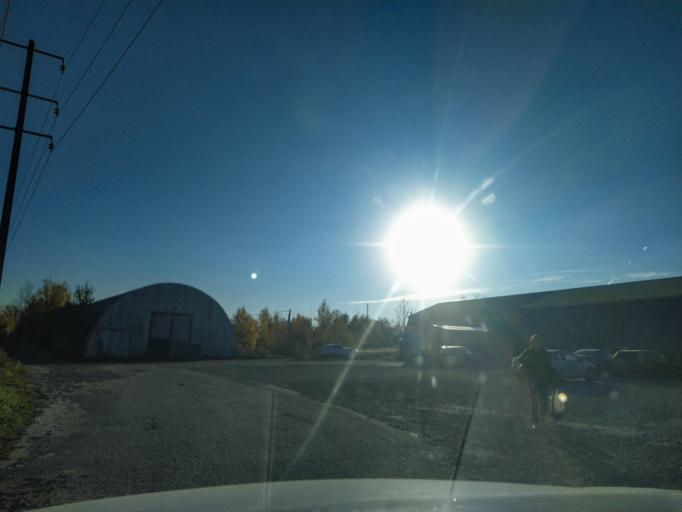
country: RU
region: Leningrad
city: Siverskiy
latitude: 59.3560
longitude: 30.0613
